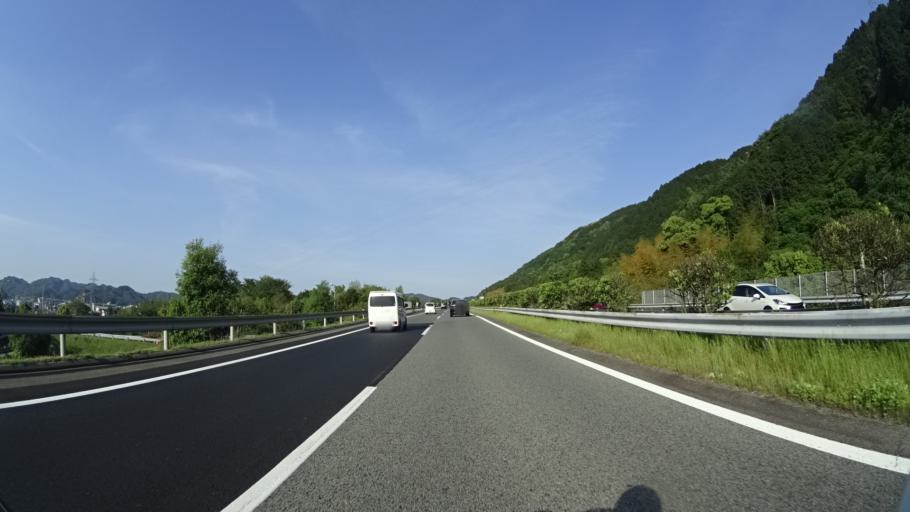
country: JP
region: Ehime
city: Niihama
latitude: 33.9264
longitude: 133.3258
